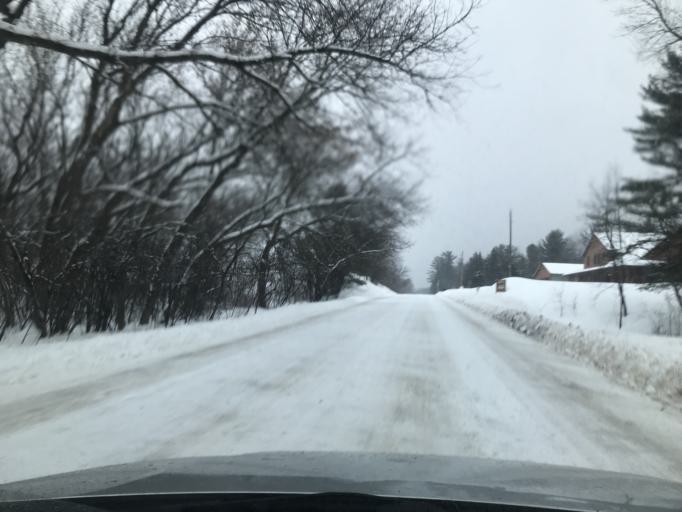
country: US
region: Wisconsin
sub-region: Marinette County
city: Peshtigo
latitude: 45.3813
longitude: -87.9437
